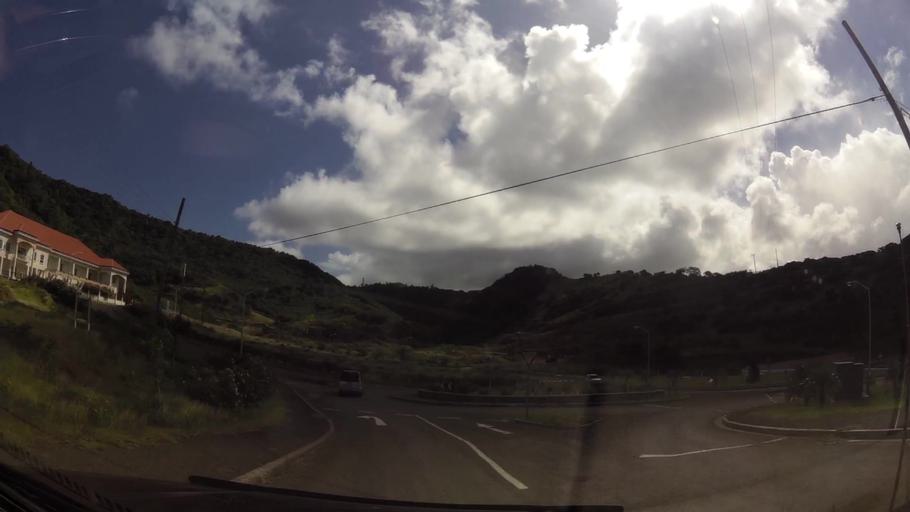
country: MS
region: Saint Peter
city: Brades
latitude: 16.7979
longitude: -62.2035
